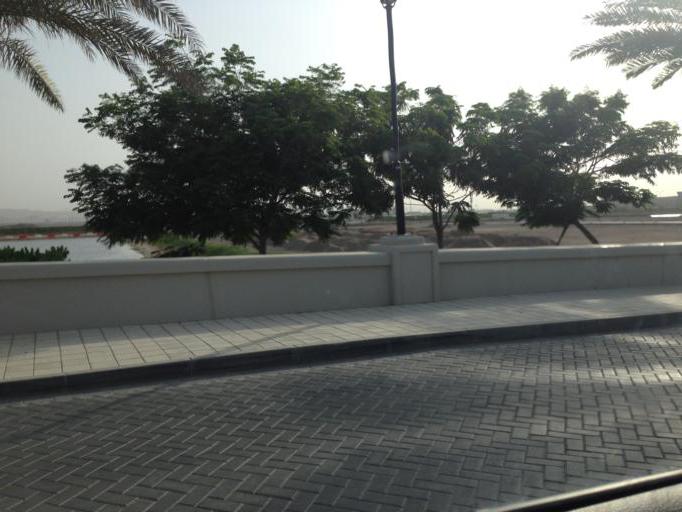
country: OM
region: Muhafazat Masqat
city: As Sib al Jadidah
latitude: 23.6221
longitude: 58.2752
